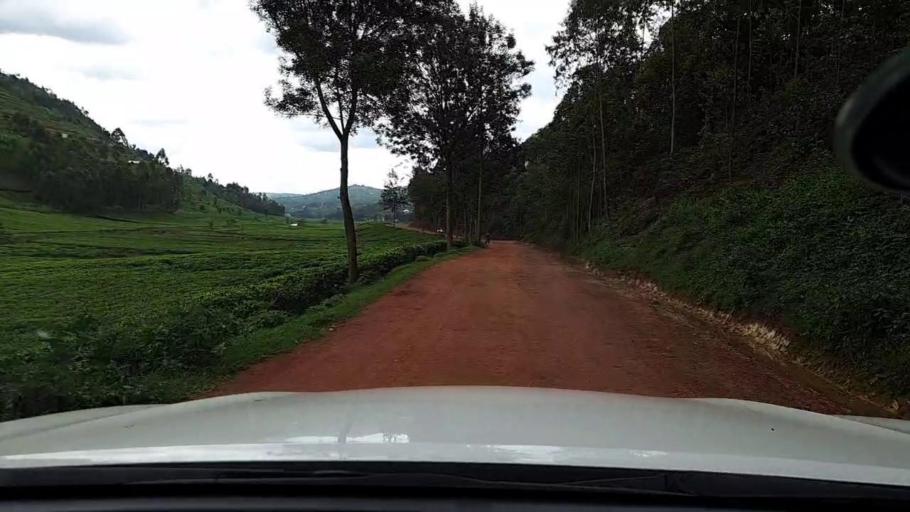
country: RW
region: Northern Province
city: Byumba
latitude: -1.6621
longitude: 29.9159
